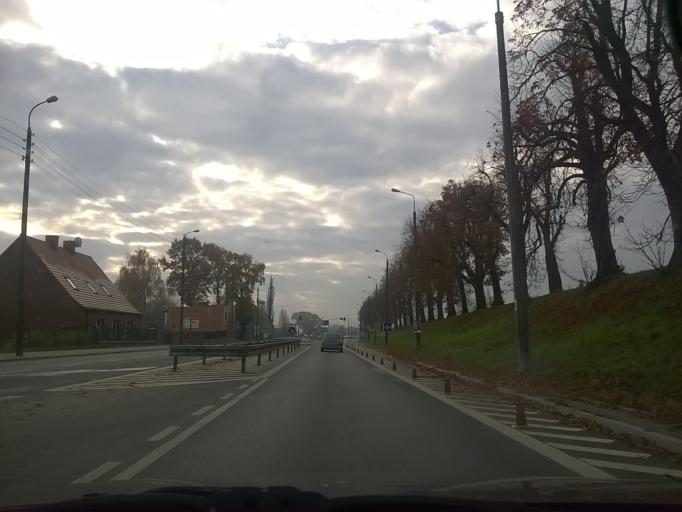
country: PL
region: Pomeranian Voivodeship
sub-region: Gdansk
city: Gdansk
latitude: 54.3126
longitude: 18.6293
